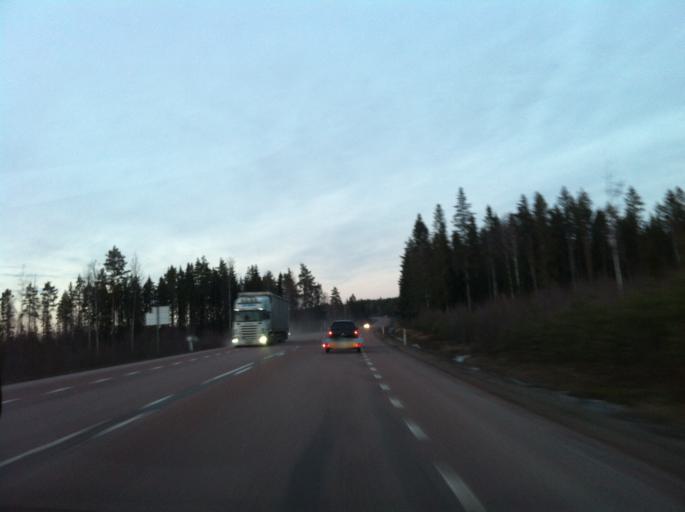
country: SE
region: Dalarna
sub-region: Mora Kommun
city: Mora
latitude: 61.0418
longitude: 14.6002
